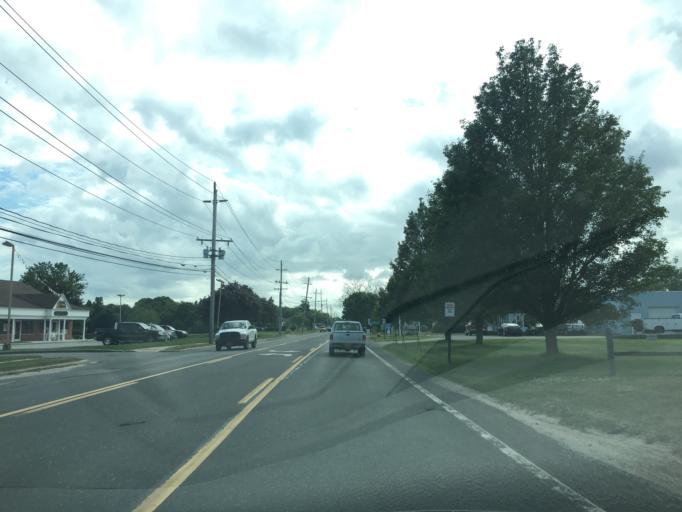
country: US
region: New York
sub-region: Suffolk County
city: Southold
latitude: 41.0738
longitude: -72.4275
